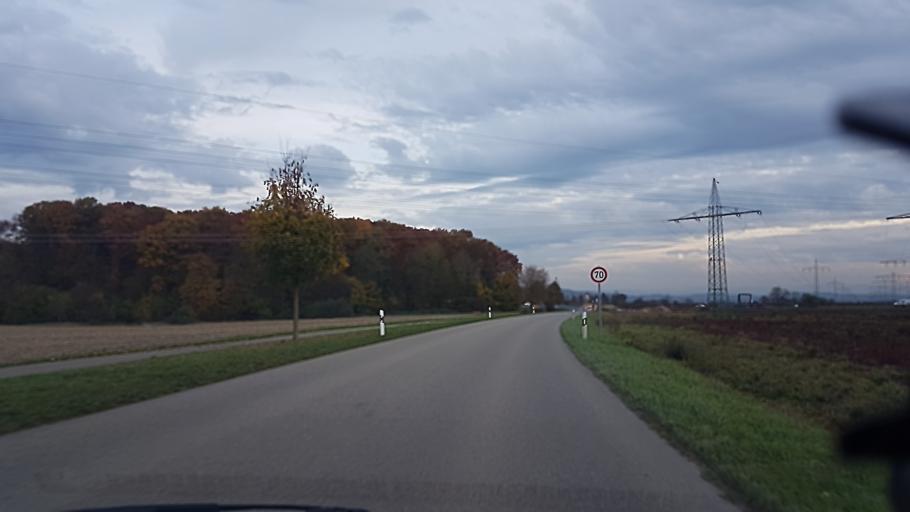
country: DE
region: Baden-Wuerttemberg
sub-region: Freiburg Region
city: Rust
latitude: 48.2620
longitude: 7.7435
